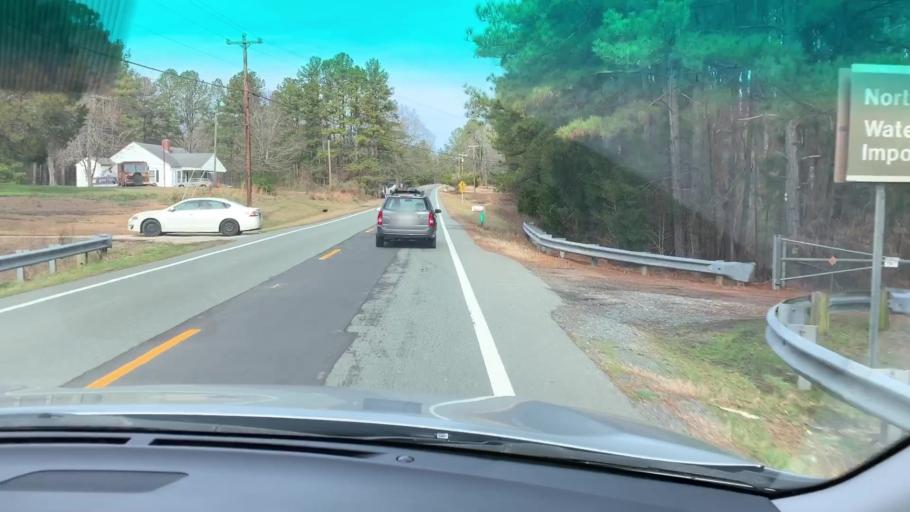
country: US
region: North Carolina
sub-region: Wake County
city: Green Level
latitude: 35.8573
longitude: -78.9403
